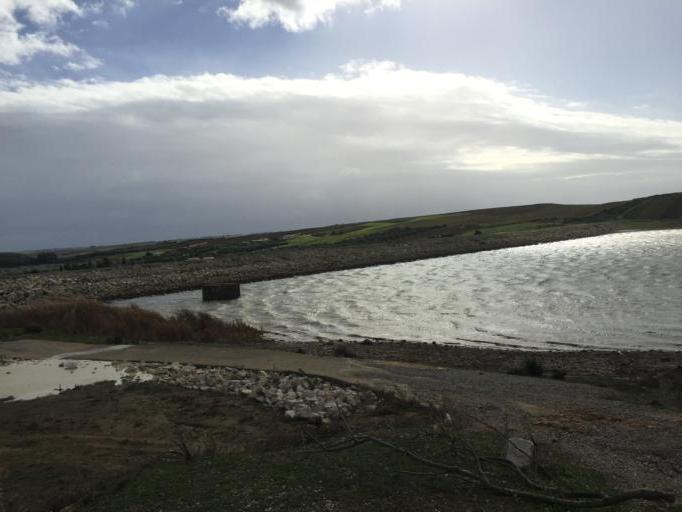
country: TN
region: Nabul
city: El Mida
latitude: 36.7908
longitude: 10.8343
